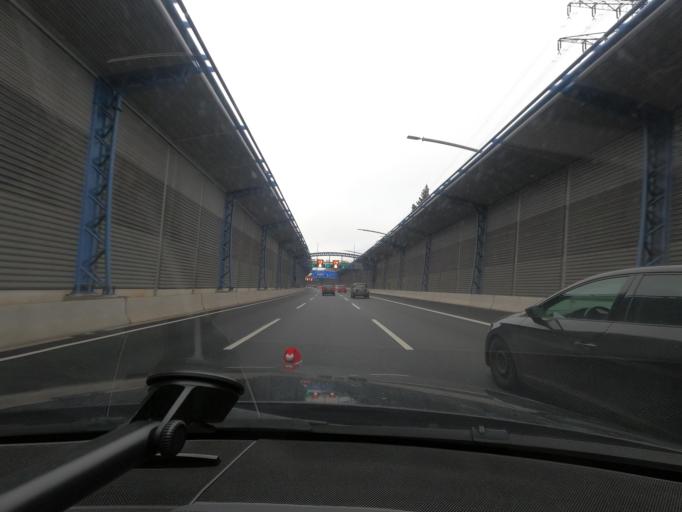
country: DE
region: Hamburg
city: Eidelstedt
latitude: 53.6266
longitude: 9.9205
